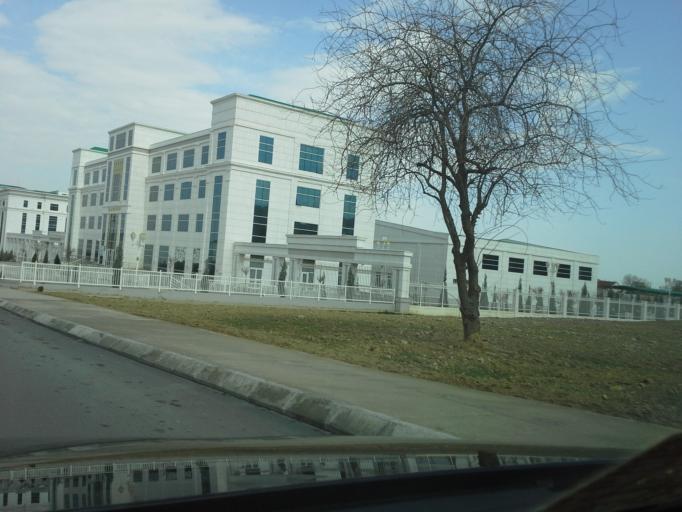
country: TM
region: Ahal
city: Ashgabat
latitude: 37.9585
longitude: 58.3240
